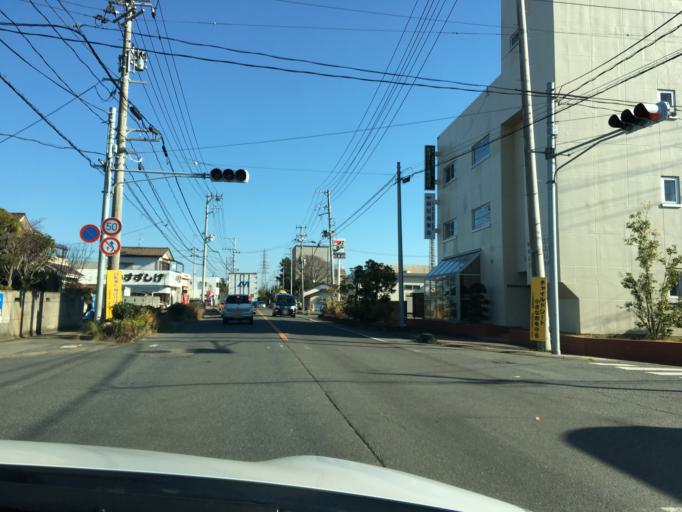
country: JP
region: Fukushima
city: Iwaki
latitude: 36.9387
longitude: 140.8636
